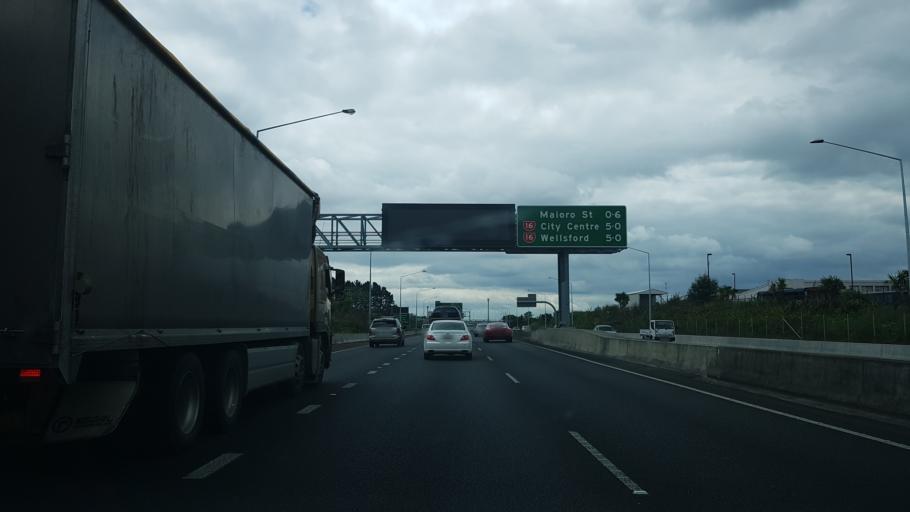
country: NZ
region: Auckland
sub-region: Auckland
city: Auckland
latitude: -36.9089
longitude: 174.7326
